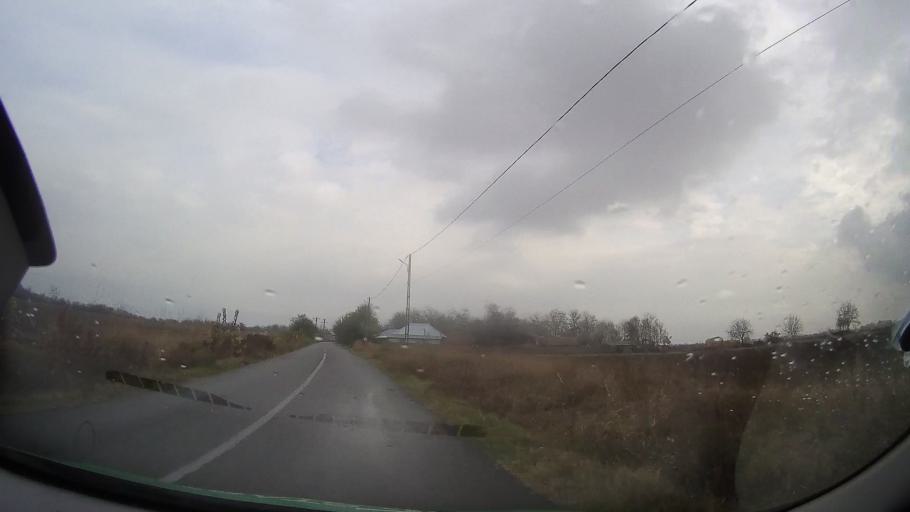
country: RO
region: Ialomita
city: Brazii
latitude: 44.7813
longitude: 26.3230
